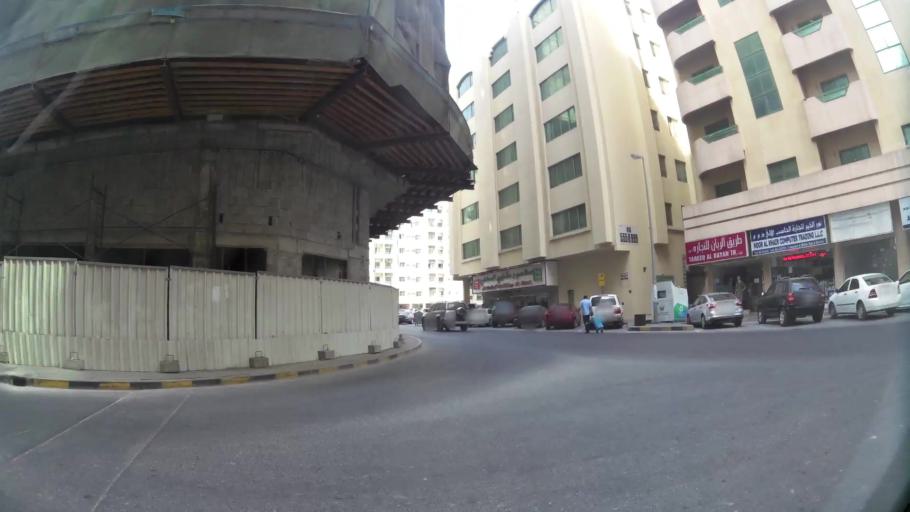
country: AE
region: Ash Shariqah
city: Sharjah
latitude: 25.3431
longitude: 55.3905
